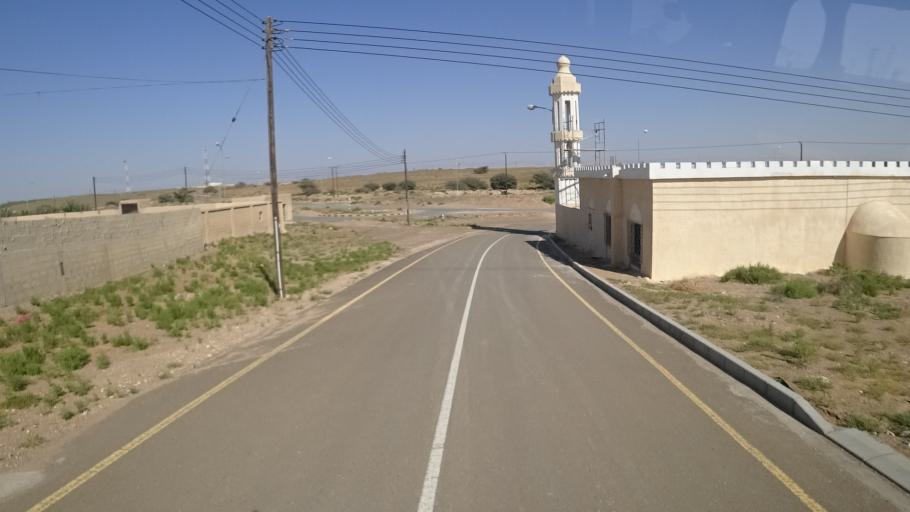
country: AE
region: Abu Dhabi
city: Al Ain
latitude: 23.9803
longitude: 55.8369
